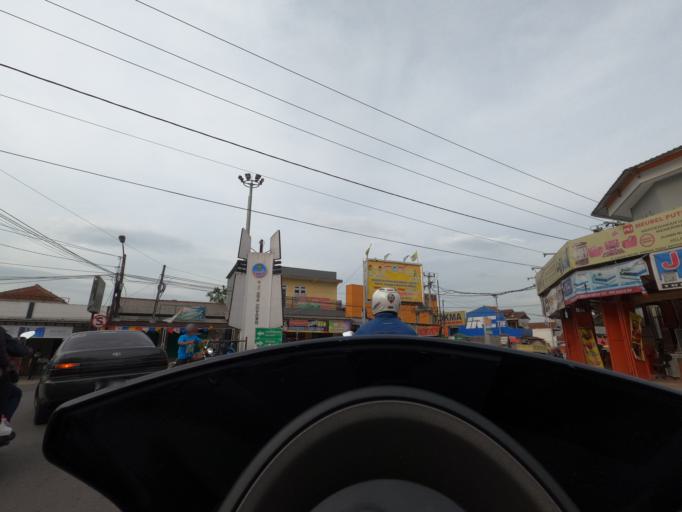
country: ID
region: West Java
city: Lembang
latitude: -6.6777
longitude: 107.6825
